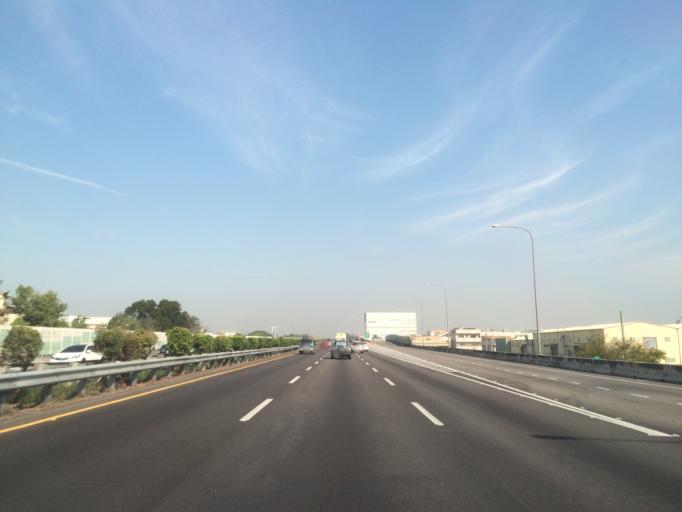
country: TW
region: Taiwan
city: Fengyuan
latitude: 24.2435
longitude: 120.6896
